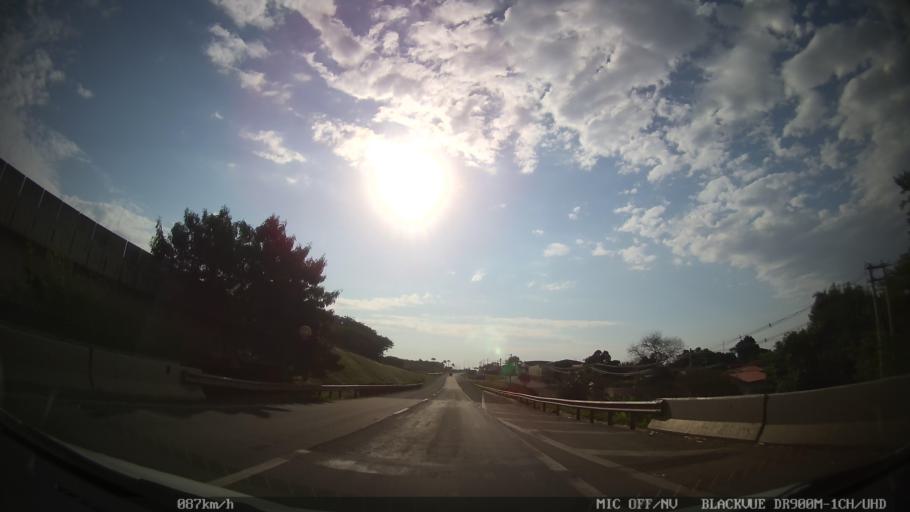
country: BR
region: Sao Paulo
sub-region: Cosmopolis
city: Cosmopolis
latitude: -22.6949
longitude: -47.1518
